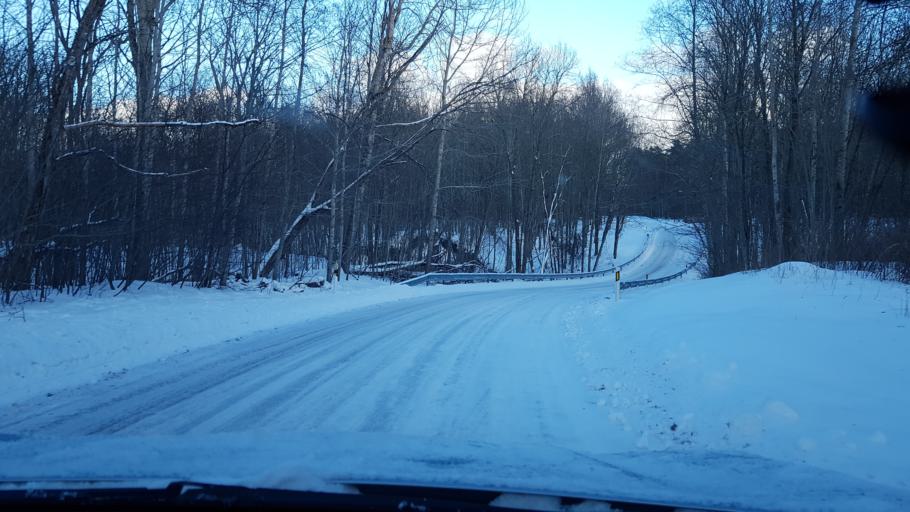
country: EE
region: Harju
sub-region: Nissi vald
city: Turba
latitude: 59.2215
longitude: 24.1419
